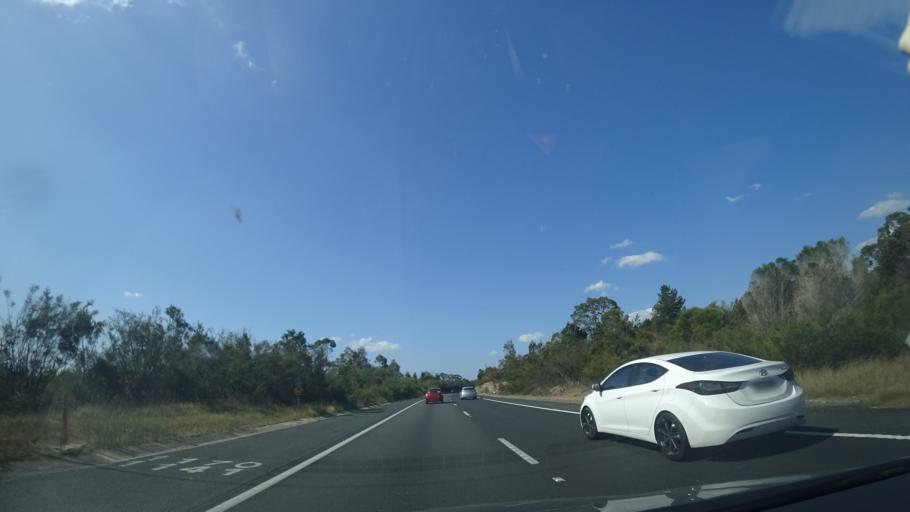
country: AU
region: New South Wales
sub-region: Wingecarribee
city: Colo Vale
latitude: -34.3521
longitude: 150.5447
